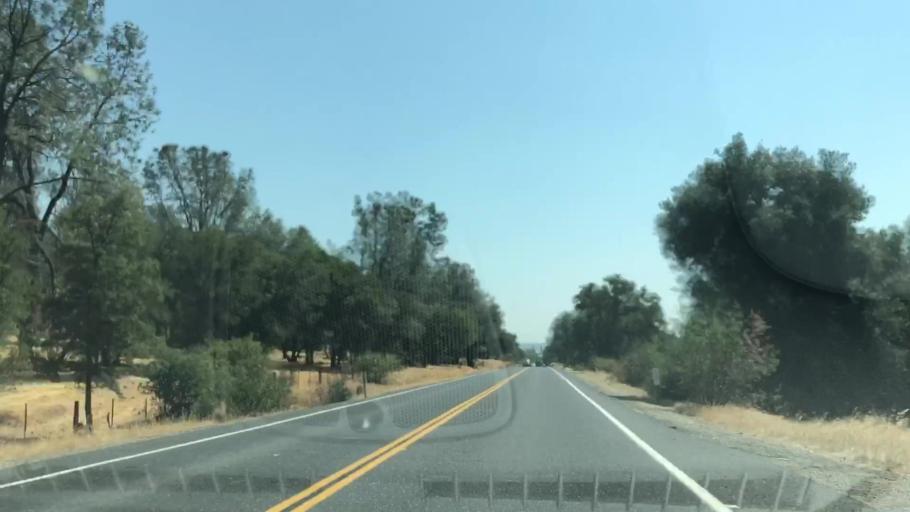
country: US
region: California
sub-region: Calaveras County
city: Copperopolis
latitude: 37.9462
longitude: -120.6090
